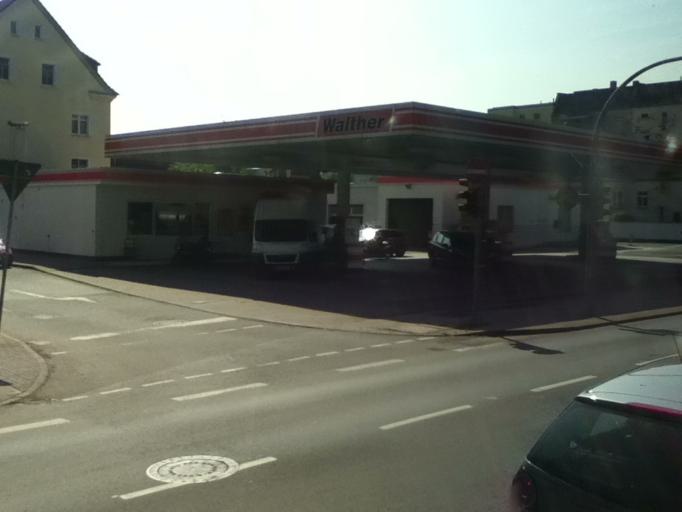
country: DE
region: Thuringia
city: Gera
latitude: 50.8860
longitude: 12.0744
